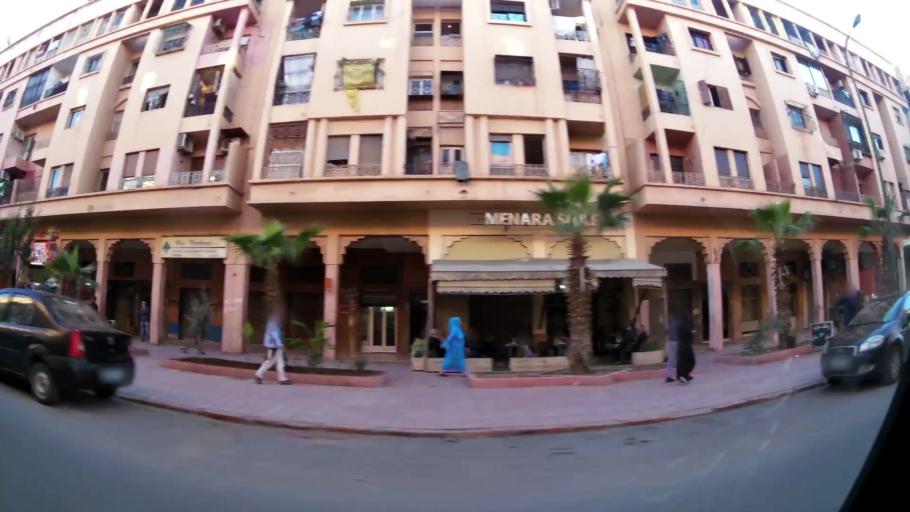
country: MA
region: Marrakech-Tensift-Al Haouz
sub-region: Marrakech
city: Marrakesh
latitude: 31.6221
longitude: -8.0283
